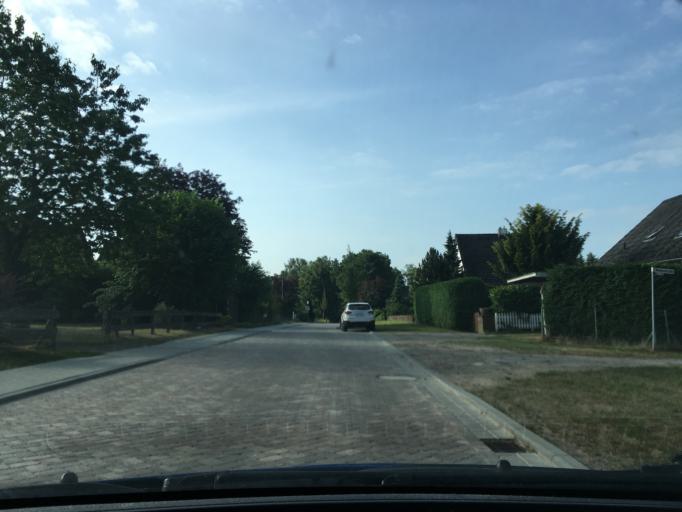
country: DE
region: Lower Saxony
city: Kakenstorf
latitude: 53.3115
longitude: 9.7737
